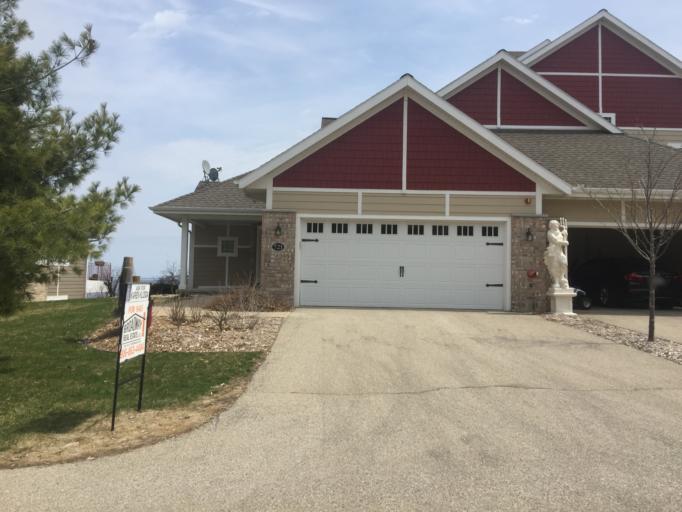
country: US
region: Wisconsin
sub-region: Marinette County
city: Marinette
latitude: 45.0697
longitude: -87.6140
